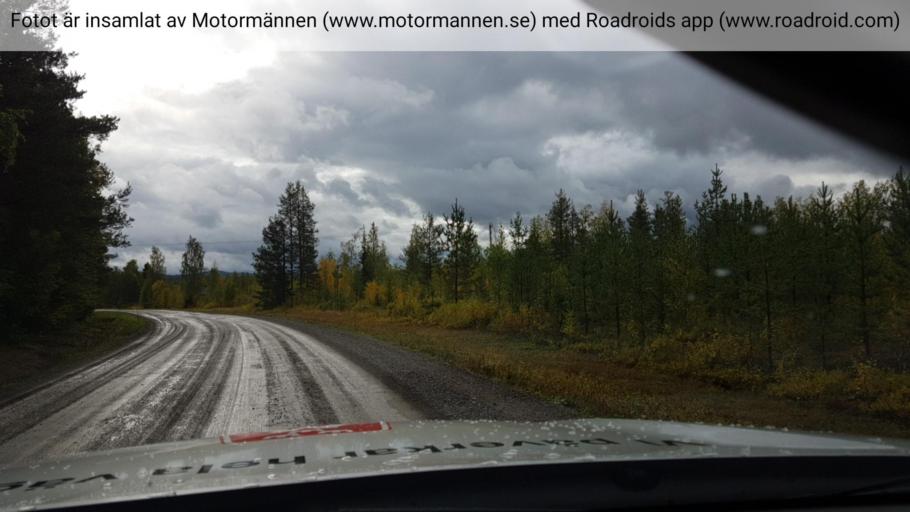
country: SE
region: Norrbotten
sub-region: Alvsbyns Kommun
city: AElvsbyn
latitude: 66.0917
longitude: 20.8918
